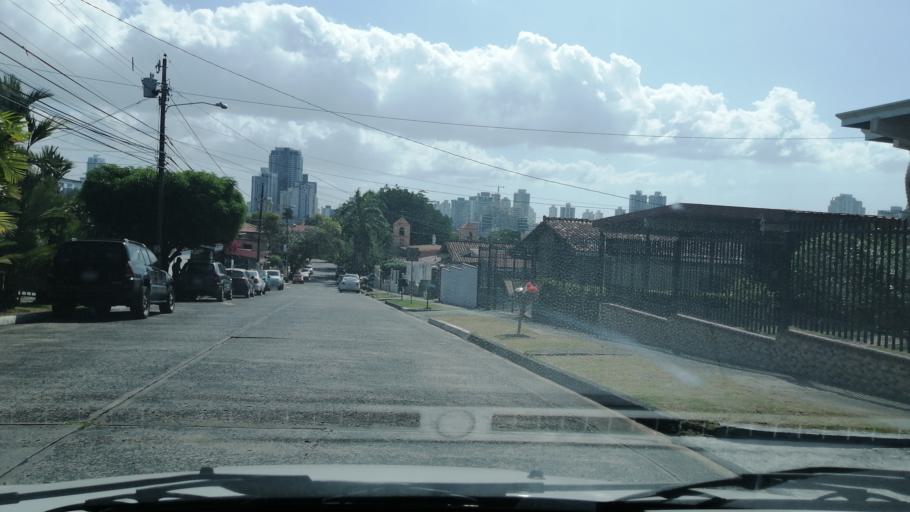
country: PA
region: Panama
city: Panama
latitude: 9.0063
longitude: -79.5263
